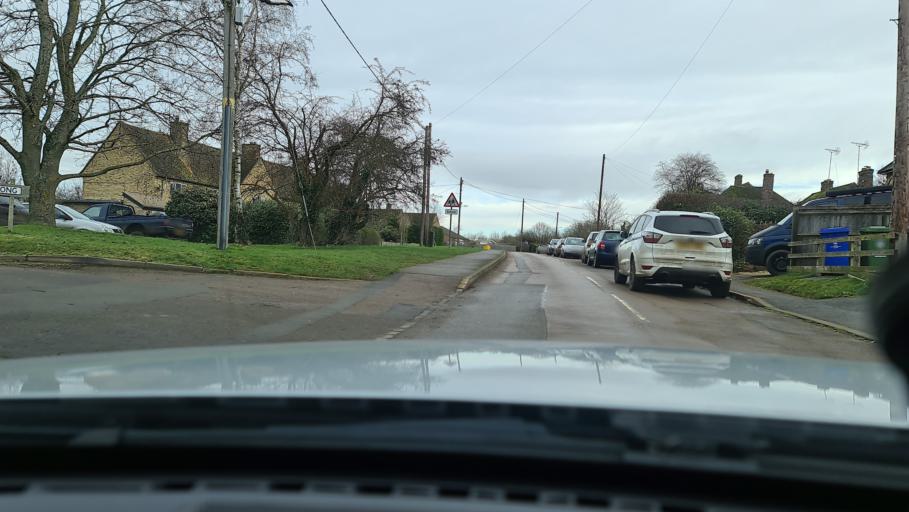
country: GB
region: England
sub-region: Oxfordshire
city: Banbury
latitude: 52.0903
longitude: -1.2802
